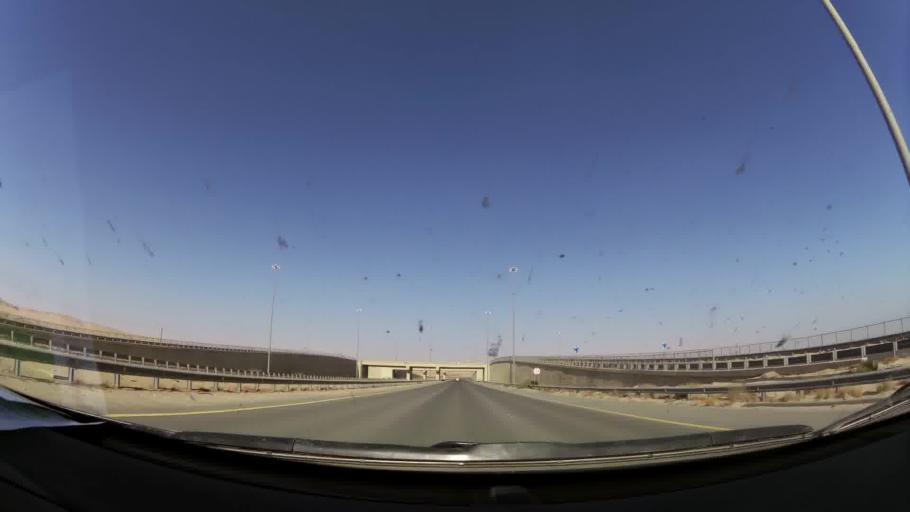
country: KW
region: Muhafazat al Jahra'
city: Al Jahra'
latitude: 29.4717
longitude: 47.7673
